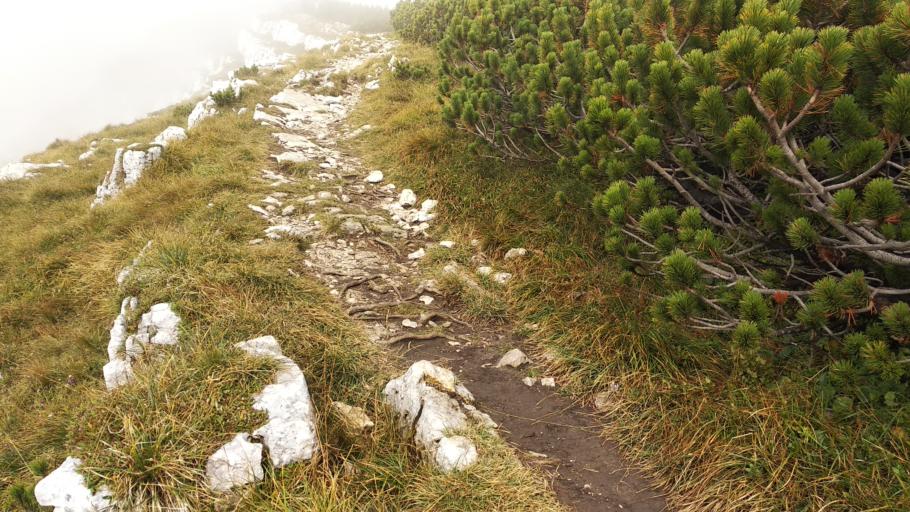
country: IT
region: Trentino-Alto Adige
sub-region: Provincia di Trento
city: Borgo
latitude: 45.9729
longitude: 11.4472
